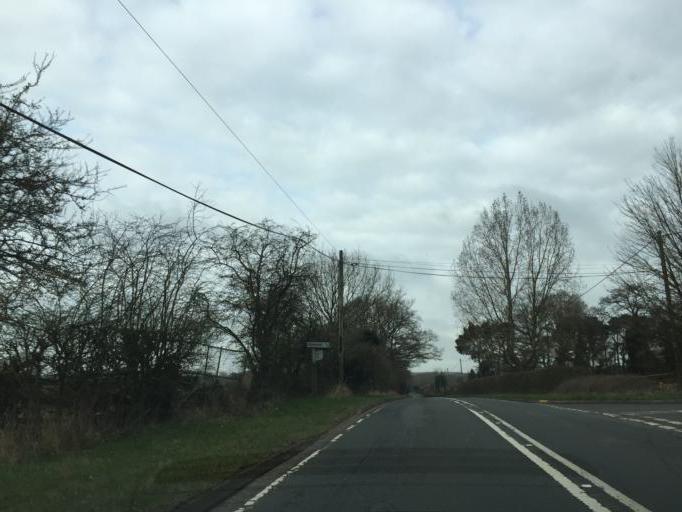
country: GB
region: England
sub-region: Warwickshire
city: Henley in Arden
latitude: 52.2991
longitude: -1.8300
